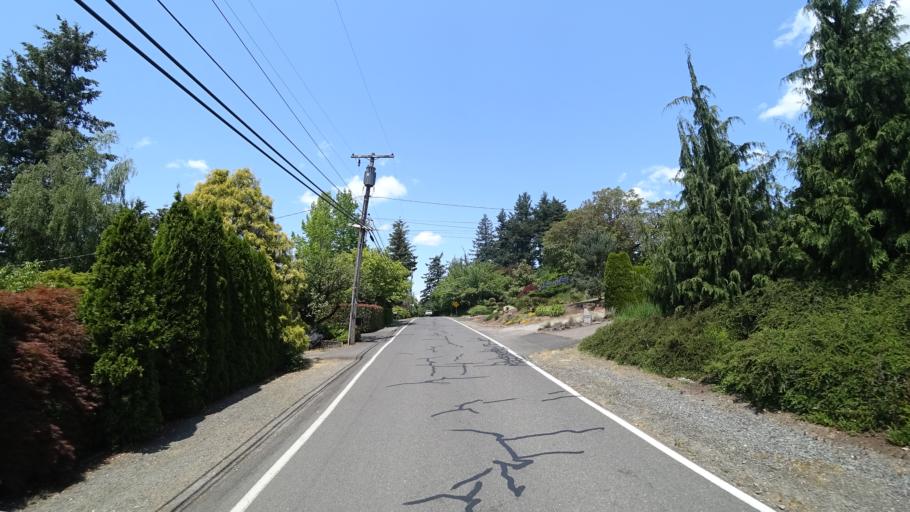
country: US
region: Oregon
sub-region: Clackamas County
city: Happy Valley
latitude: 45.4492
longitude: -122.5496
